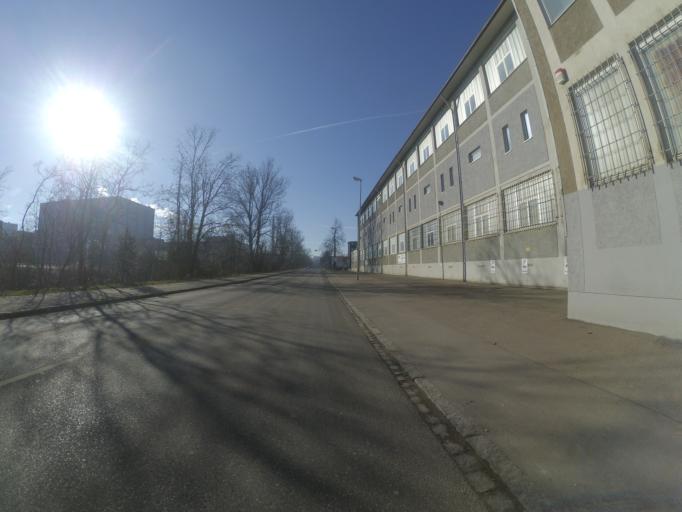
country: DE
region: Baden-Wuerttemberg
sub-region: Tuebingen Region
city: Ulm
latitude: 48.3699
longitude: 9.9537
